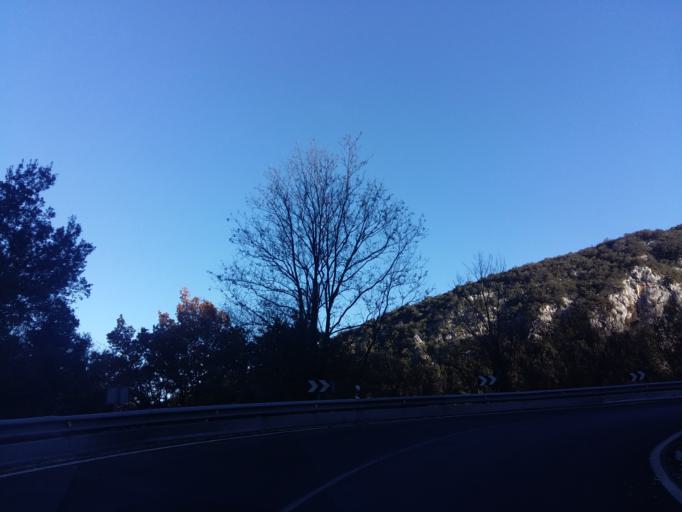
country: ES
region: Cantabria
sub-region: Provincia de Cantabria
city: Ramales de la Victoria
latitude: 43.2461
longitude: -3.4596
